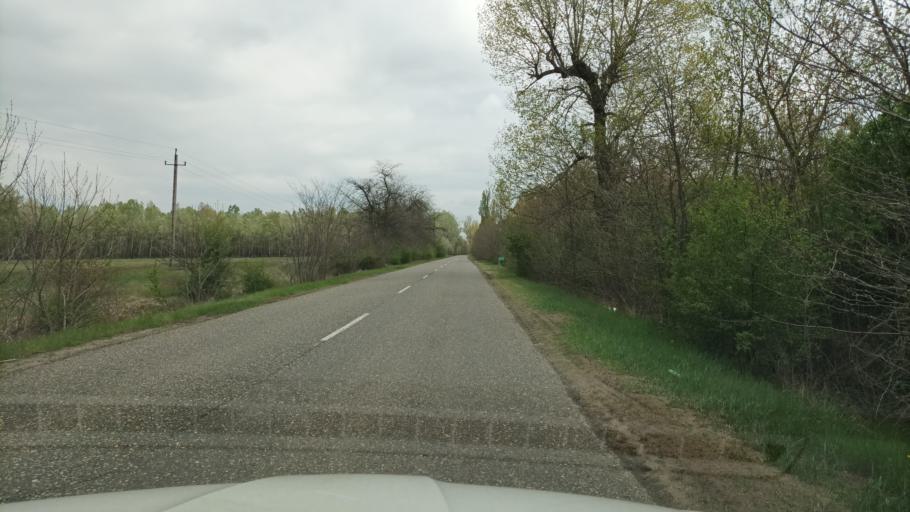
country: HU
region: Pest
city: Tortel
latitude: 47.0876
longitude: 19.8779
